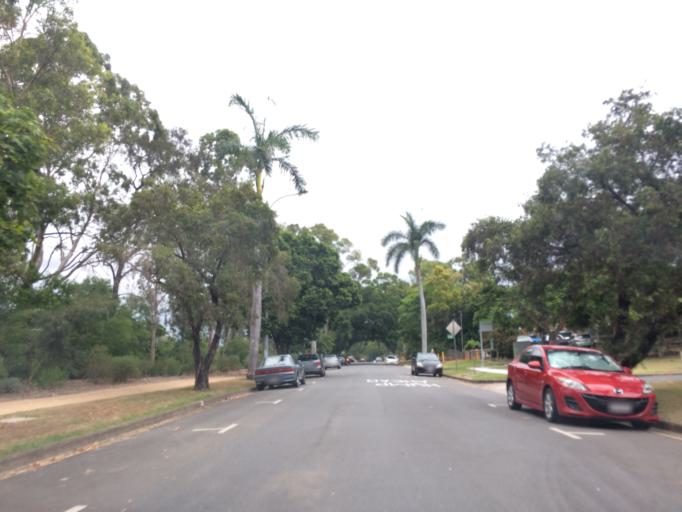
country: AU
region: Queensland
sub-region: Brisbane
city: Yeronga
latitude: -27.5021
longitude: 153.0163
